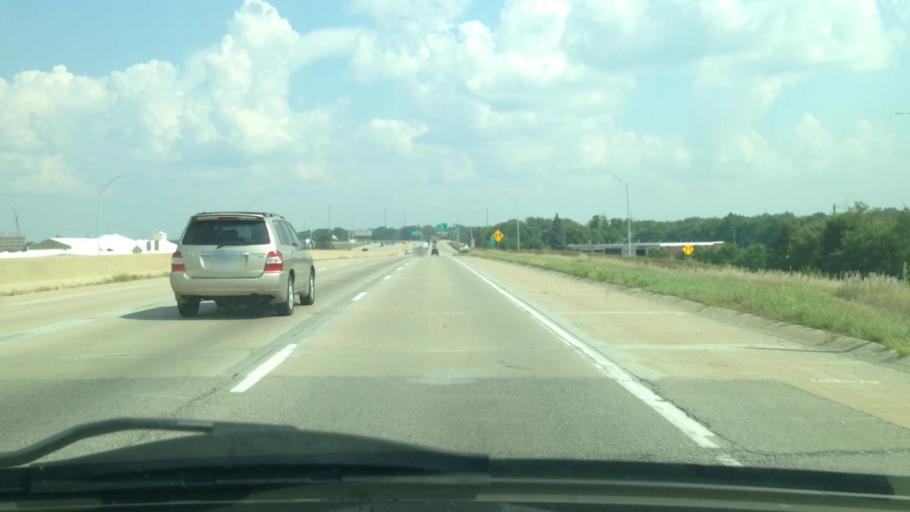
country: US
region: Iowa
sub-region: Black Hawk County
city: Waterloo
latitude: 42.5024
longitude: -92.3664
